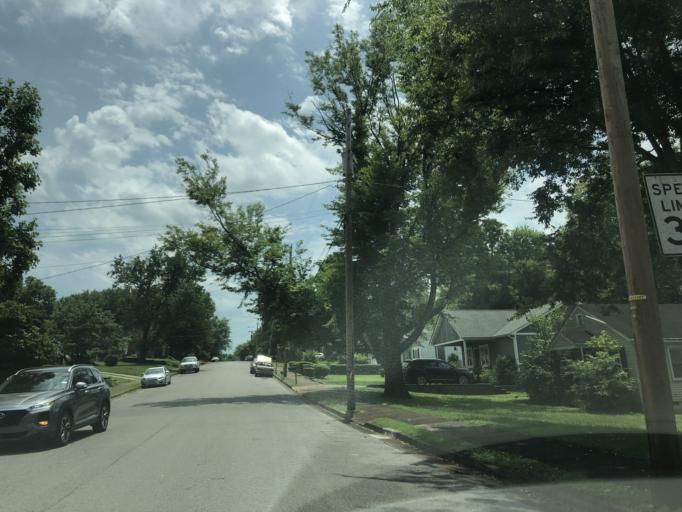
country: US
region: Tennessee
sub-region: Davidson County
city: Nashville
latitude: 36.1845
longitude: -86.7571
